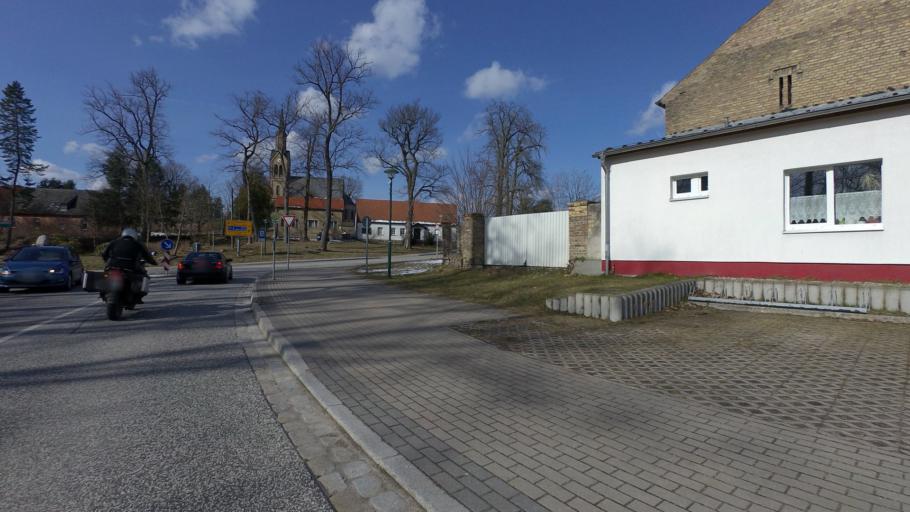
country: DE
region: Brandenburg
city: Rudnitz
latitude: 52.7605
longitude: 13.5654
